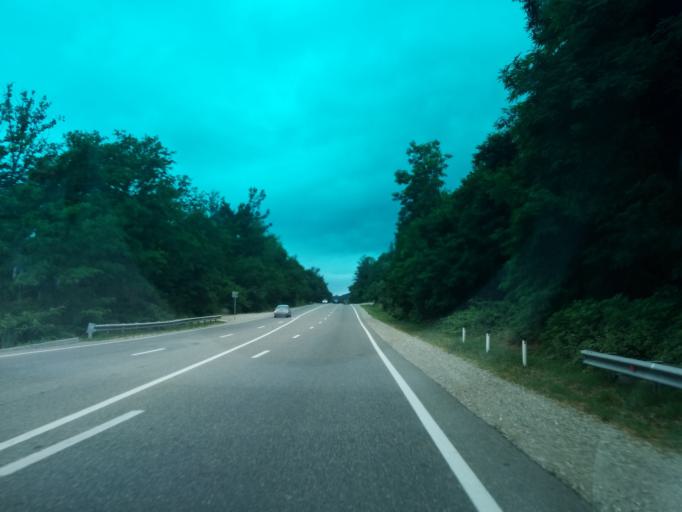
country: RU
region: Krasnodarskiy
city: Ol'ginka
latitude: 44.1789
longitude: 38.9396
